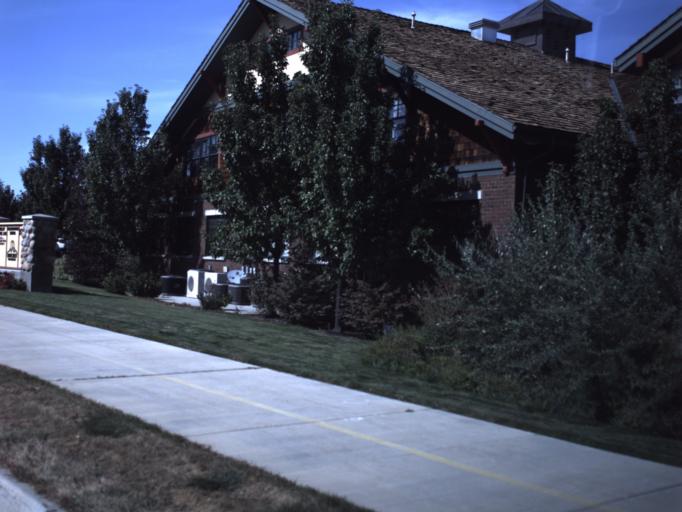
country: US
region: Utah
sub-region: Salt Lake County
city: South Jordan
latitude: 40.5621
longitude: -111.9269
